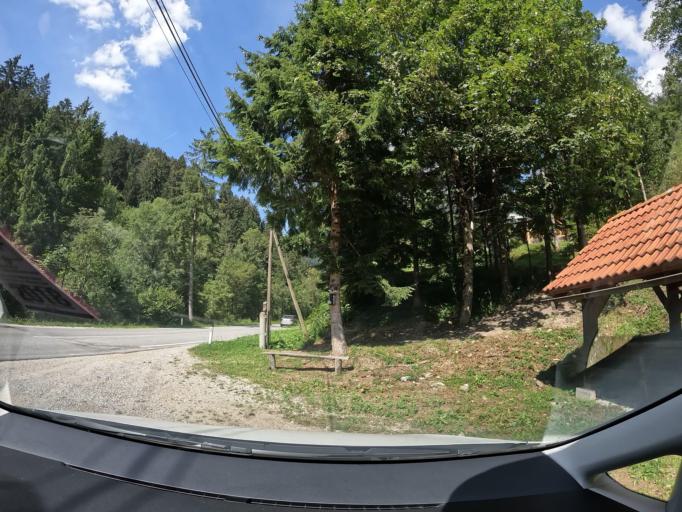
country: SI
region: Jezersko
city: Zgornje Jezersko
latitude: 46.3289
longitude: 14.4914
